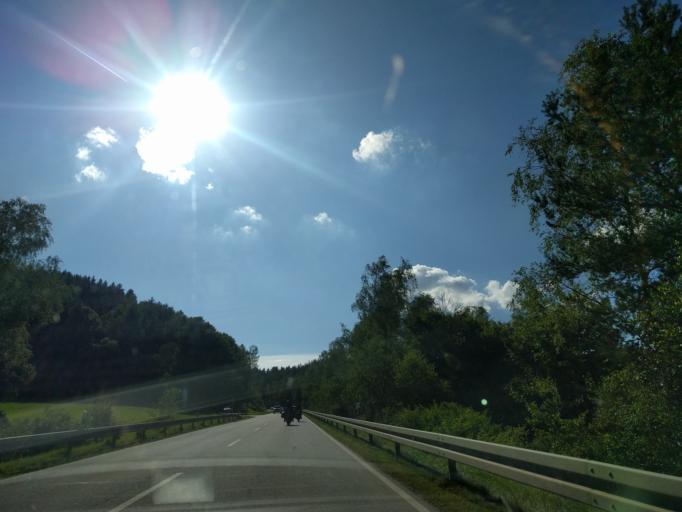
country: DE
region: Bavaria
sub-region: Lower Bavaria
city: Bischofsmais
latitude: 48.9062
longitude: 13.1055
